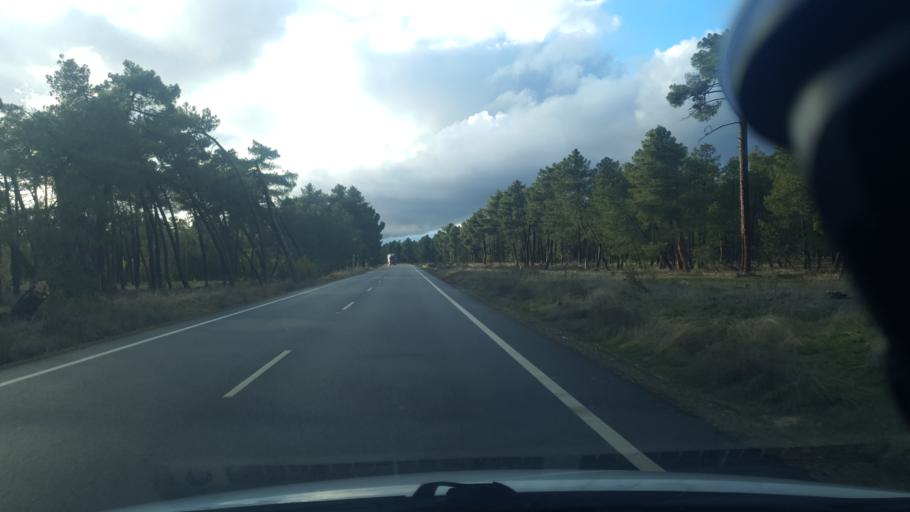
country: ES
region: Castille and Leon
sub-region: Provincia de Segovia
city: Nava de la Asuncion
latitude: 41.1558
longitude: -4.5184
